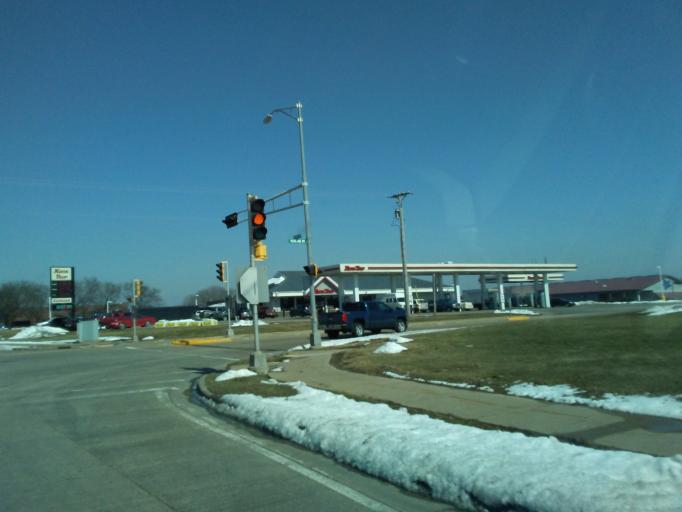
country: US
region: Wisconsin
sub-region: Vernon County
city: Viroqua
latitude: 43.5746
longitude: -90.8888
